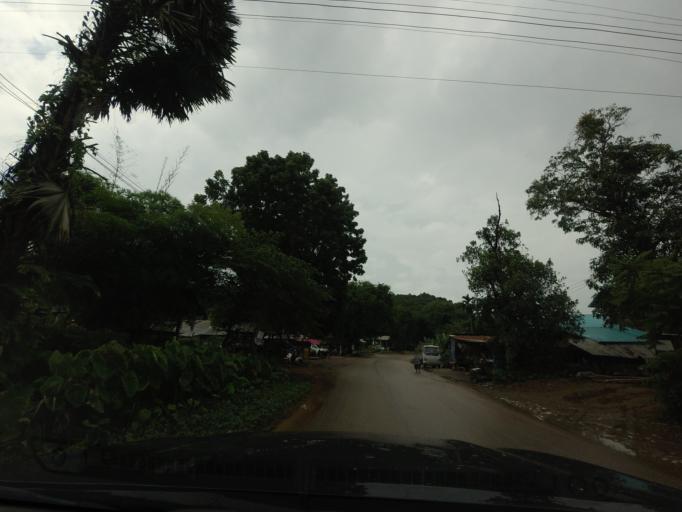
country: TH
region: Loei
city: Pak Chom
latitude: 18.1107
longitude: 101.9838
